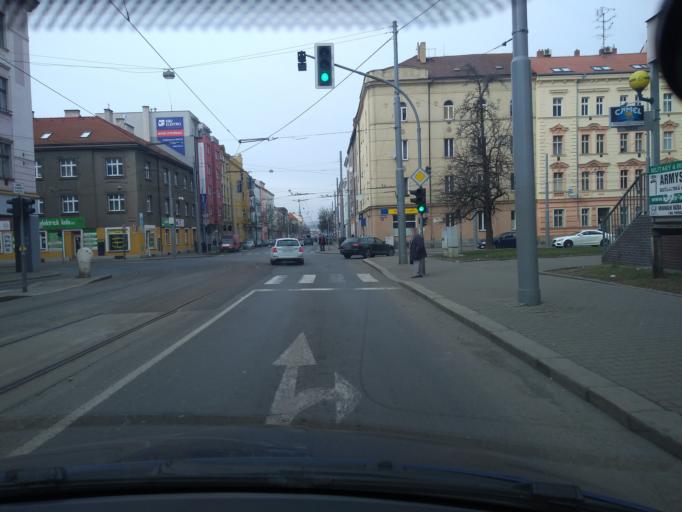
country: CZ
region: Plzensky
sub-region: Okres Plzen-Mesto
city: Pilsen
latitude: 49.7394
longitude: 13.3923
